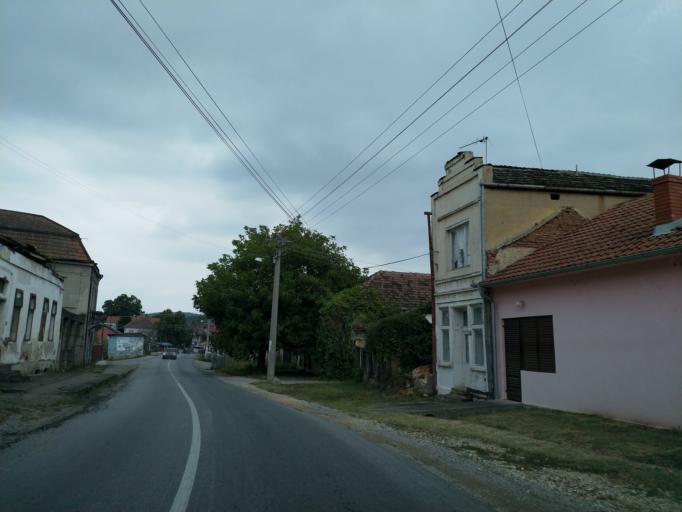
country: RS
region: Central Serbia
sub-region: Pomoravski Okrug
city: Jagodina
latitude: 44.0670
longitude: 21.1794
